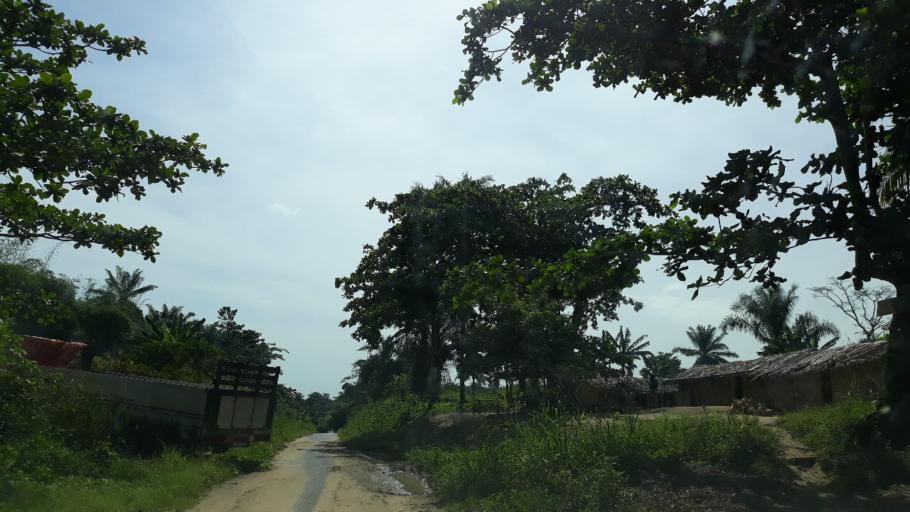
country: CD
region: Maniema
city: Kindu
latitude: -2.9071
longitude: 26.0301
